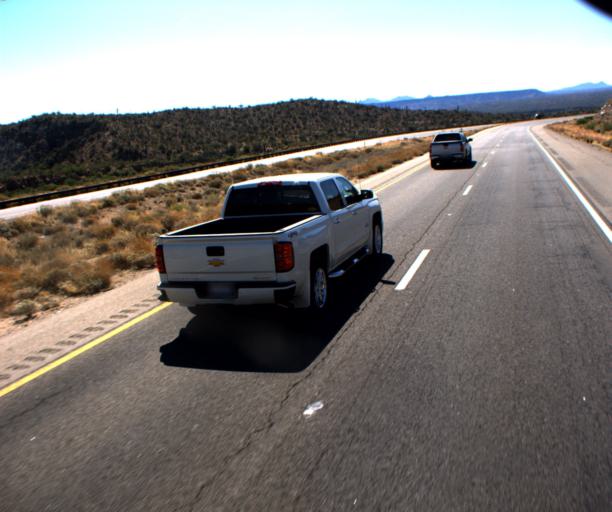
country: US
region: Arizona
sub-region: Yavapai County
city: Bagdad
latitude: 34.3960
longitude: -113.2128
